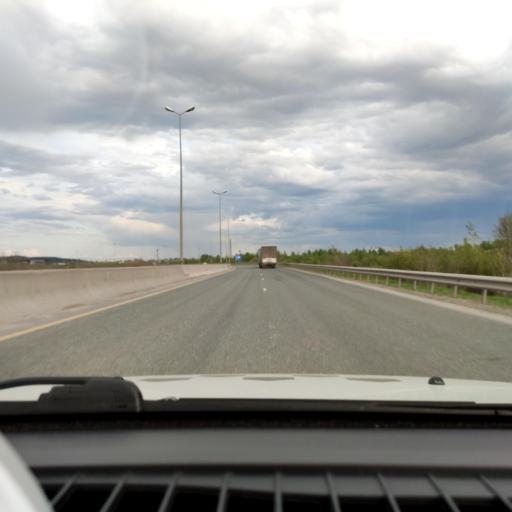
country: RU
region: Perm
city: Kondratovo
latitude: 57.9598
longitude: 56.1086
